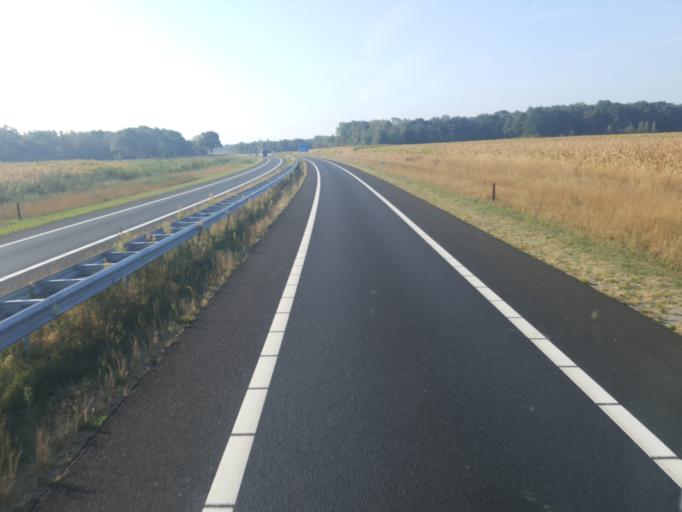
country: NL
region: Gelderland
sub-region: Berkelland
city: Eibergen
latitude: 52.0971
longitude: 6.6208
